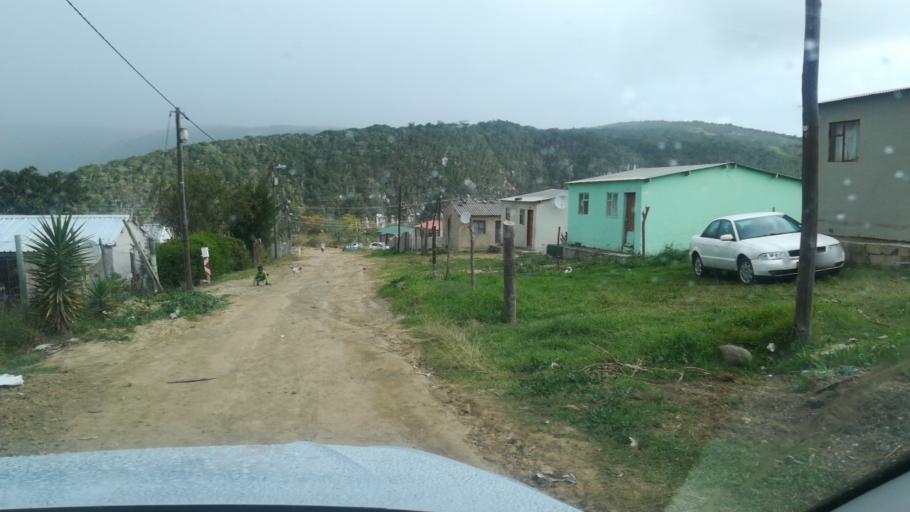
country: ZA
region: Eastern Cape
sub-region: Buffalo City Metropolitan Municipality
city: East London
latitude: -32.9945
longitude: 27.7987
